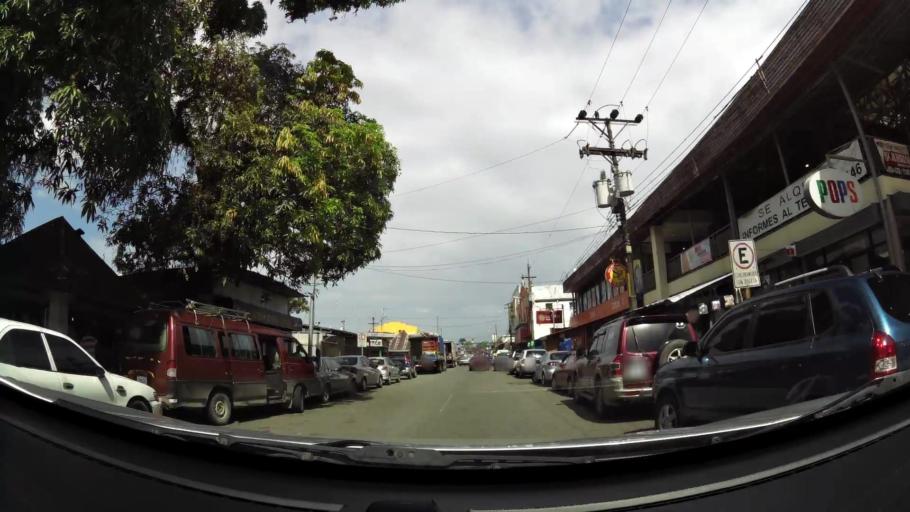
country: CR
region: Limon
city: Limon
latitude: 9.9924
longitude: -83.0281
